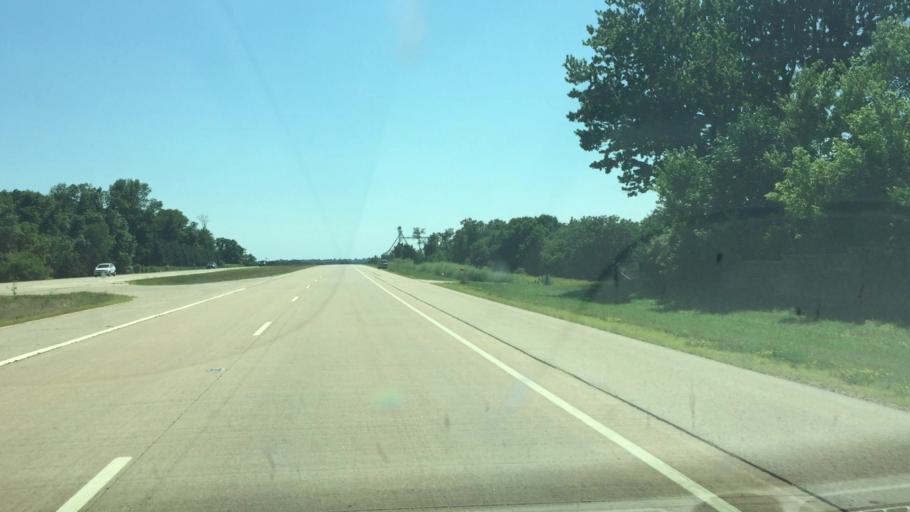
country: US
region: Wisconsin
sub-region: Grant County
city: Dickeyville
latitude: 42.6801
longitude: -90.5404
